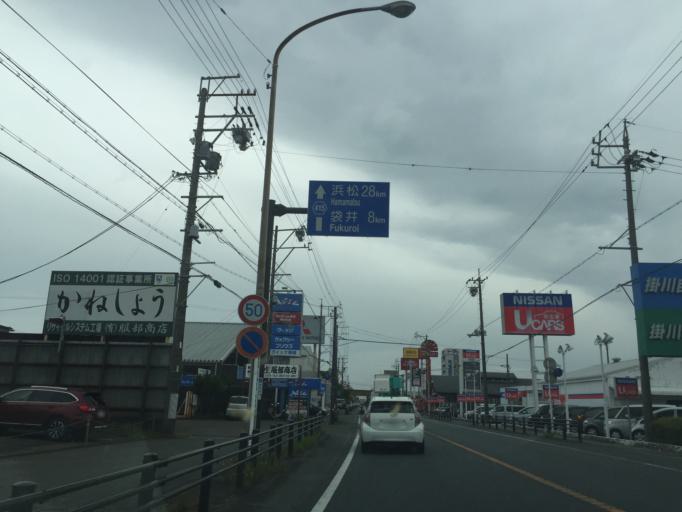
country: JP
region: Shizuoka
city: Kakegawa
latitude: 34.7749
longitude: 137.9906
